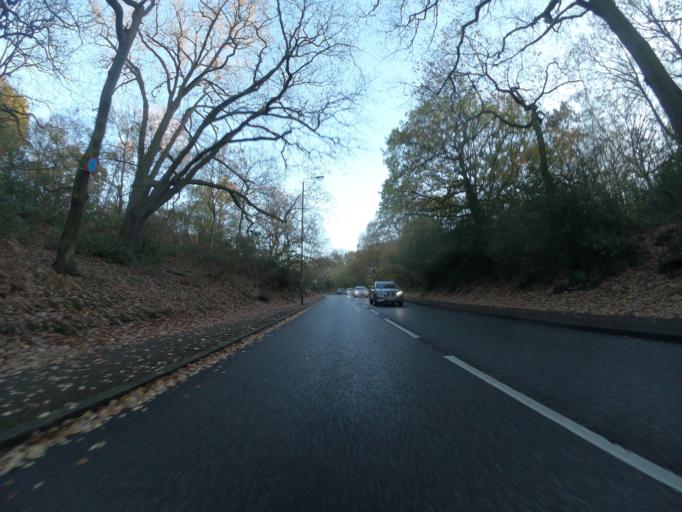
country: GB
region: England
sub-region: Greater London
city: Abbey Wood
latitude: 51.4829
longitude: 0.1111
